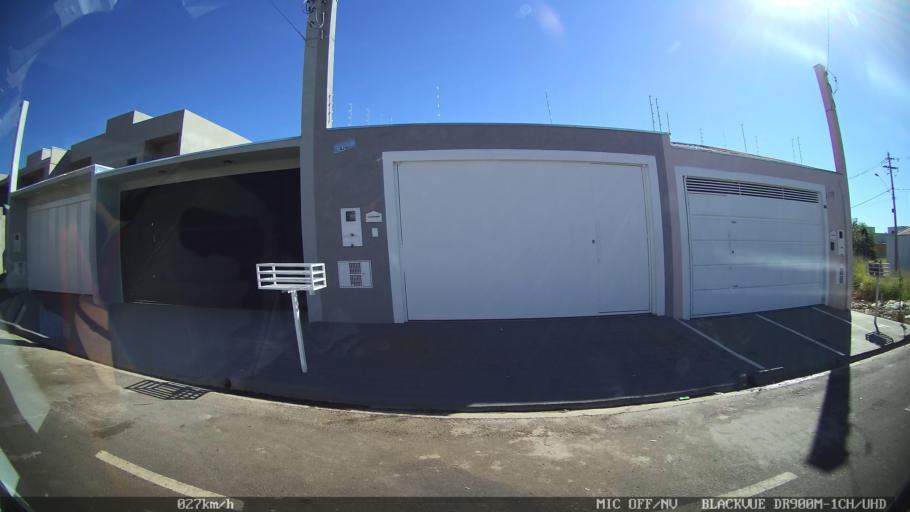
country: BR
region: Sao Paulo
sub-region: Franca
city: Franca
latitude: -20.5671
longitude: -47.3451
